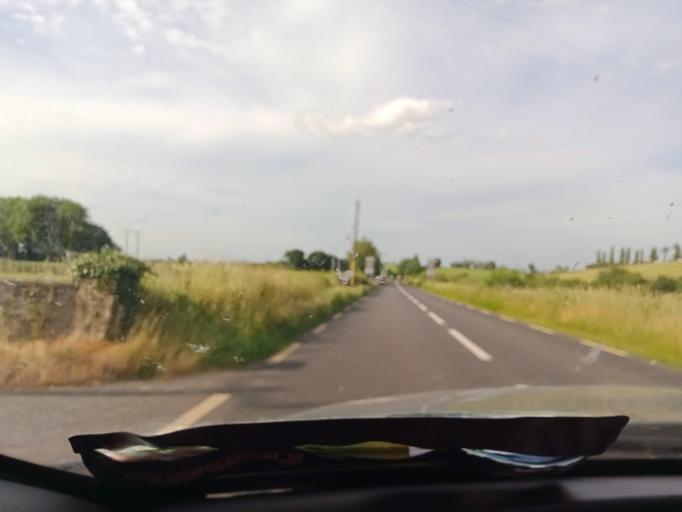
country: IE
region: Leinster
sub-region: An Longfort
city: Granard
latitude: 53.8626
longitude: -7.4412
